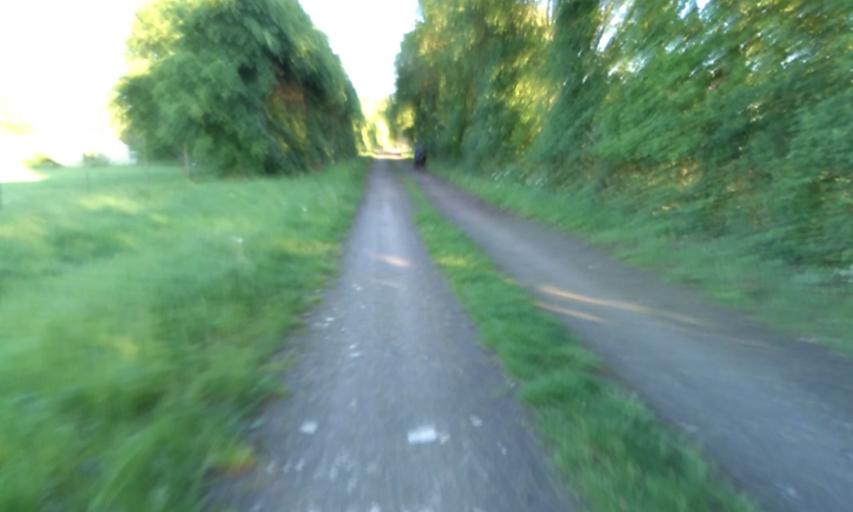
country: DE
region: Lower Saxony
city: Bliedersdorf
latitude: 53.4897
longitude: 9.5693
